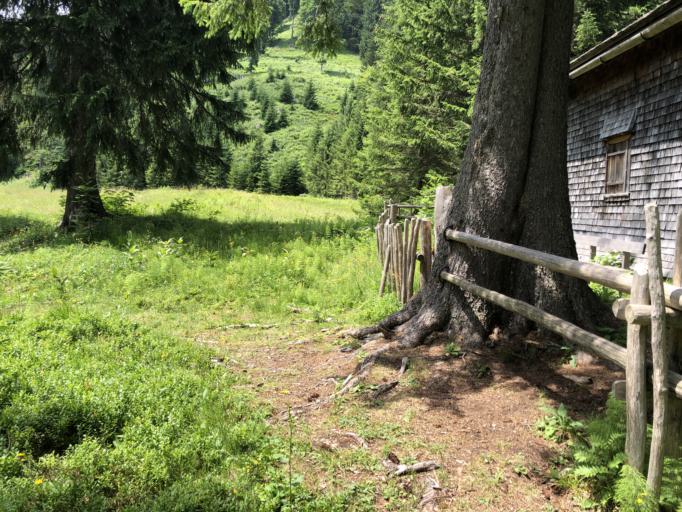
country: AT
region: Vorarlberg
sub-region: Politischer Bezirk Bregenz
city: Reuthe
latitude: 47.3282
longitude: 9.8835
